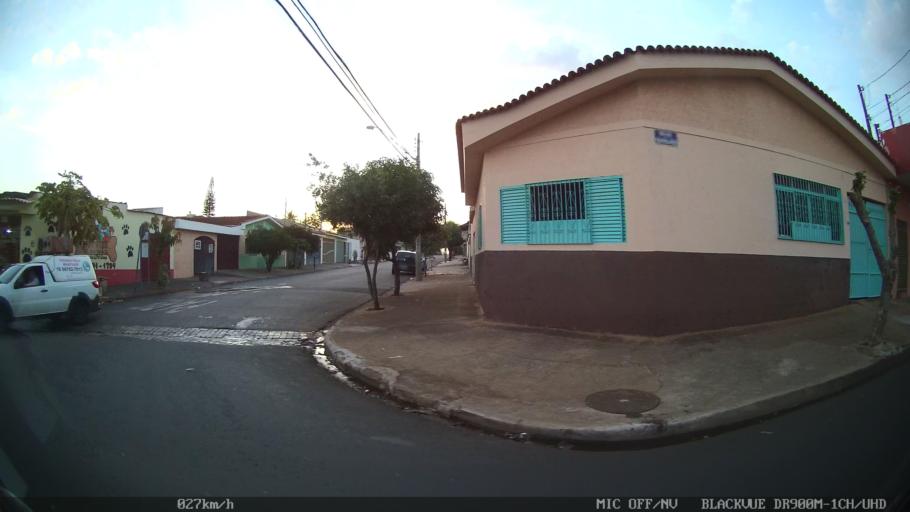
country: BR
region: Sao Paulo
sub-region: Ribeirao Preto
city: Ribeirao Preto
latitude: -21.1555
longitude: -47.8310
